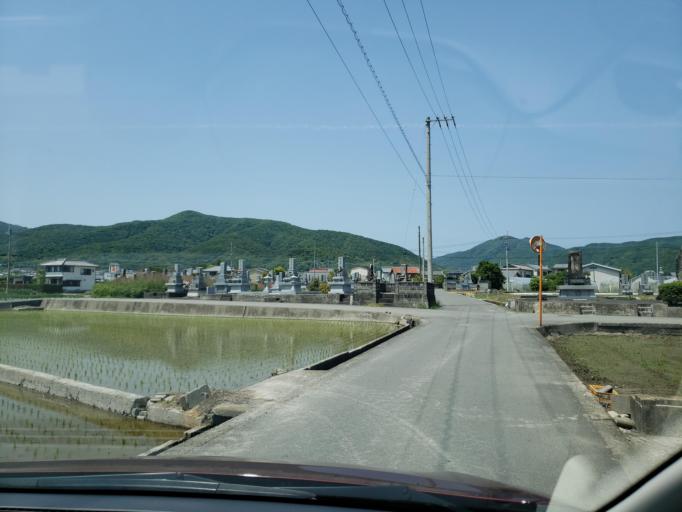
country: JP
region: Tokushima
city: Kamojimacho-jogejima
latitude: 34.0937
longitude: 134.2683
